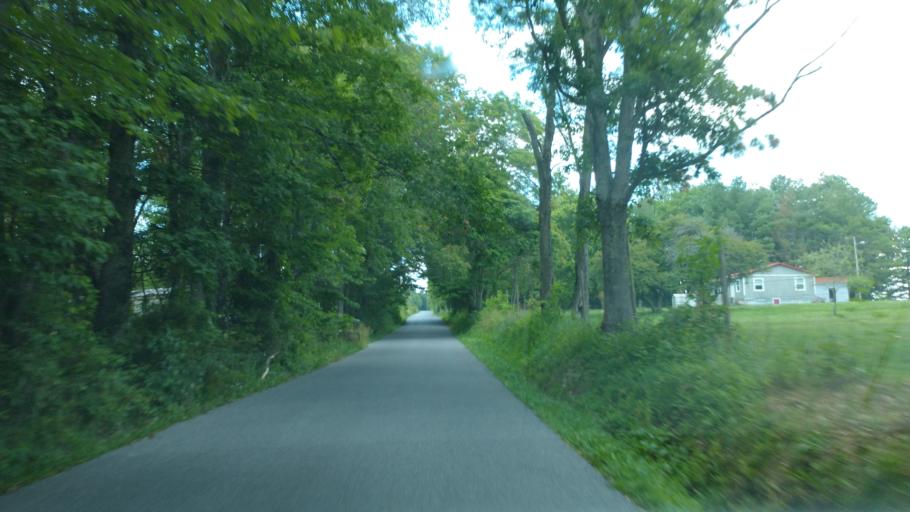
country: US
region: West Virginia
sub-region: Mercer County
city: Athens
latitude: 37.4576
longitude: -81.0422
